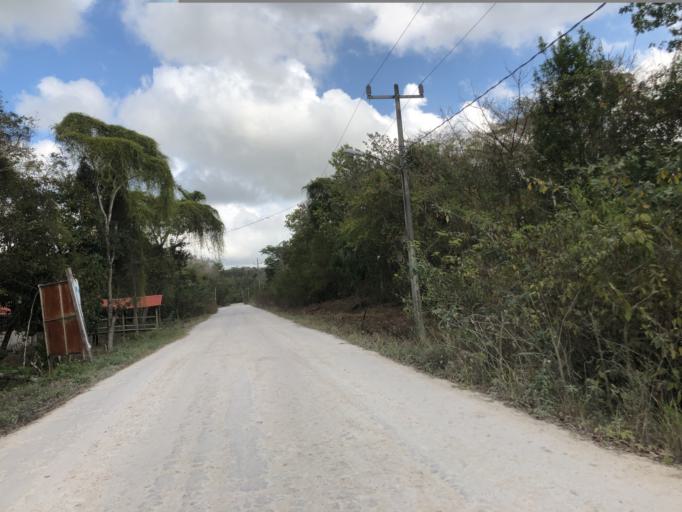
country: MX
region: Quintana Roo
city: Nicolas Bravo
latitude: 18.4571
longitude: -89.3056
